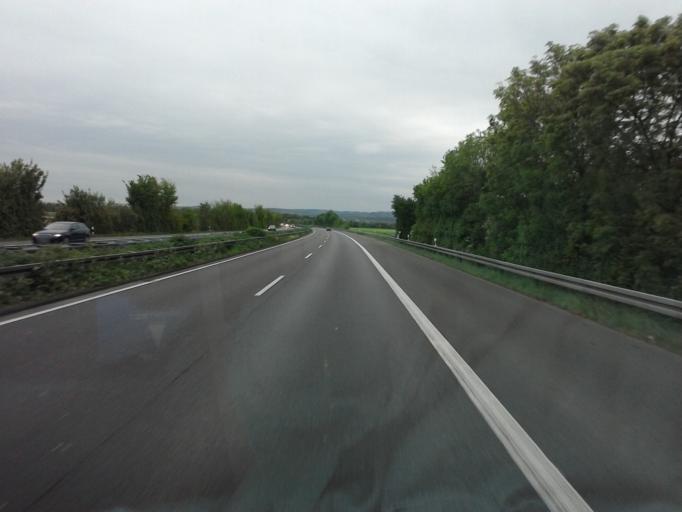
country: DE
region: North Rhine-Westphalia
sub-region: Regierungsbezirk Koln
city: Rheinbach
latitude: 50.6615
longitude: 6.9236
